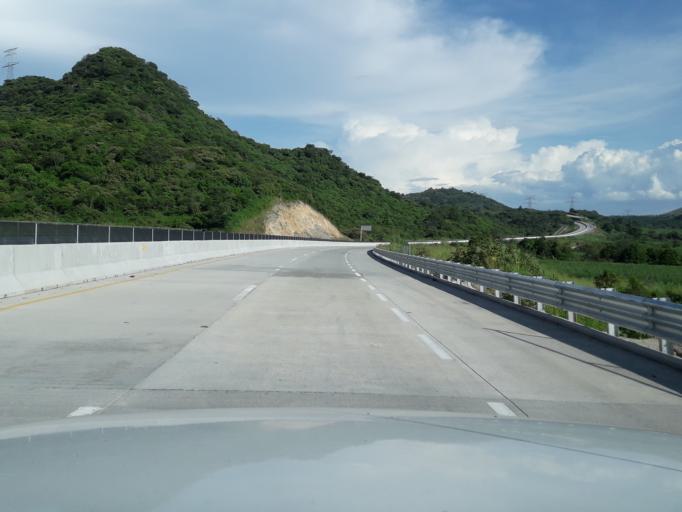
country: MX
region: Jalisco
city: Tala
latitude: 20.5972
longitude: -103.6740
